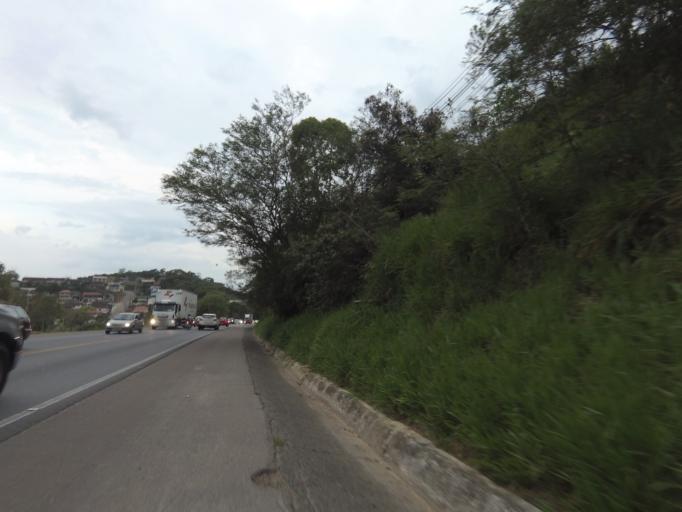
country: BR
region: Santa Catarina
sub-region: Blumenau
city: Blumenau
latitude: -26.8593
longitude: -49.0580
